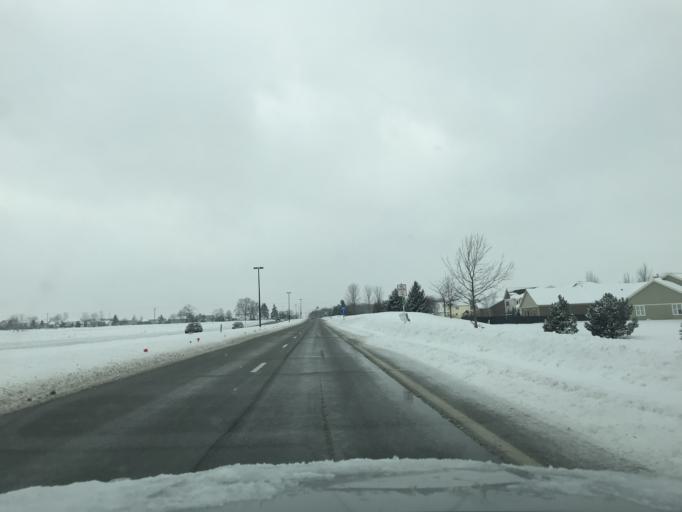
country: US
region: Wisconsin
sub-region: Dane County
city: Sun Prairie
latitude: 43.1650
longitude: -89.2798
